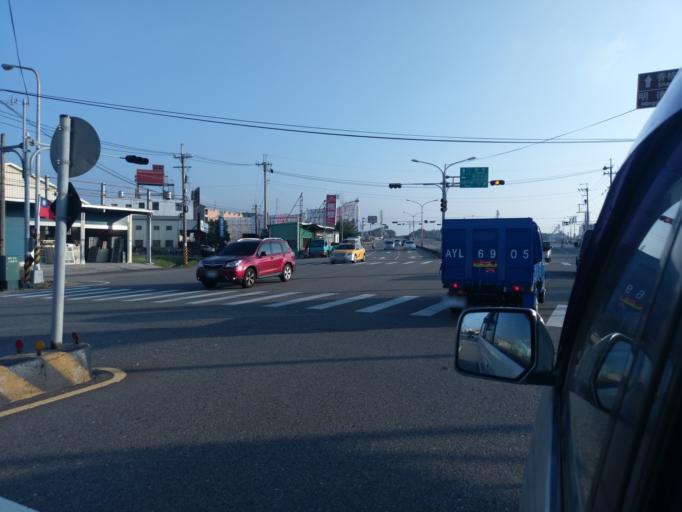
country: TW
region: Taiwan
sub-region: Miaoli
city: Miaoli
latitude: 24.6705
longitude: 120.8823
